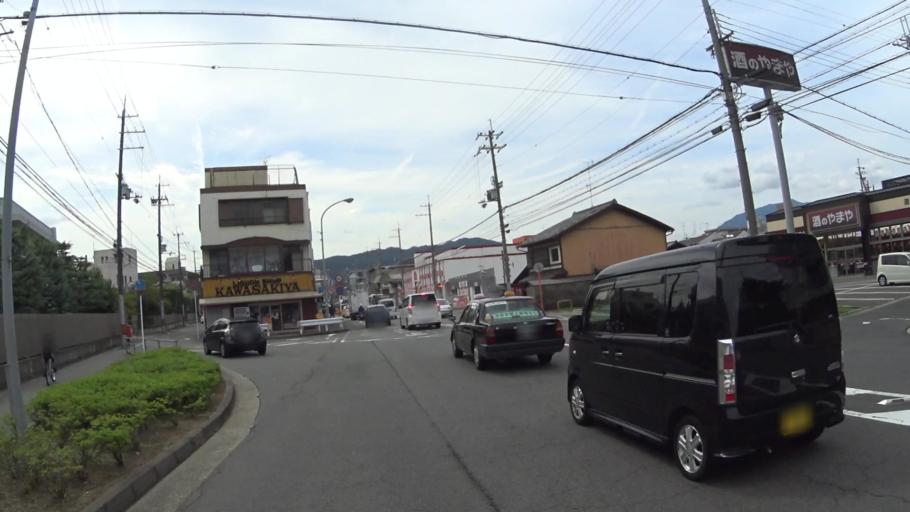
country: JP
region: Kyoto
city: Muko
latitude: 35.0038
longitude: 135.7082
